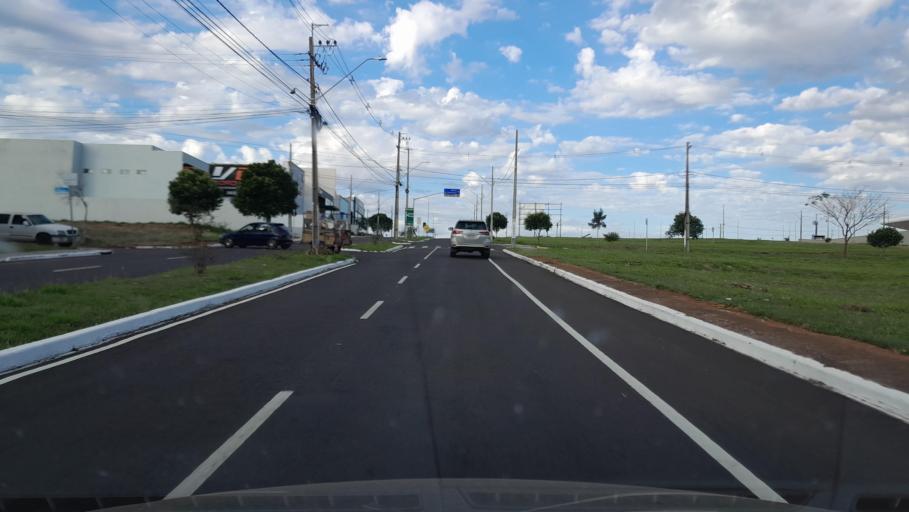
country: BR
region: Parana
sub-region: Umuarama
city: Umuarama
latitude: -23.7528
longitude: -53.2749
